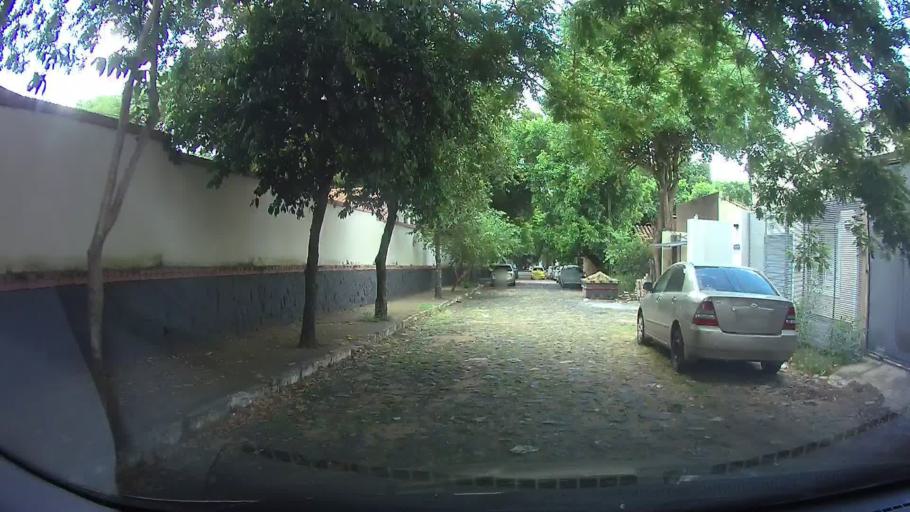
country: PY
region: Asuncion
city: Asuncion
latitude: -25.2949
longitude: -57.6016
